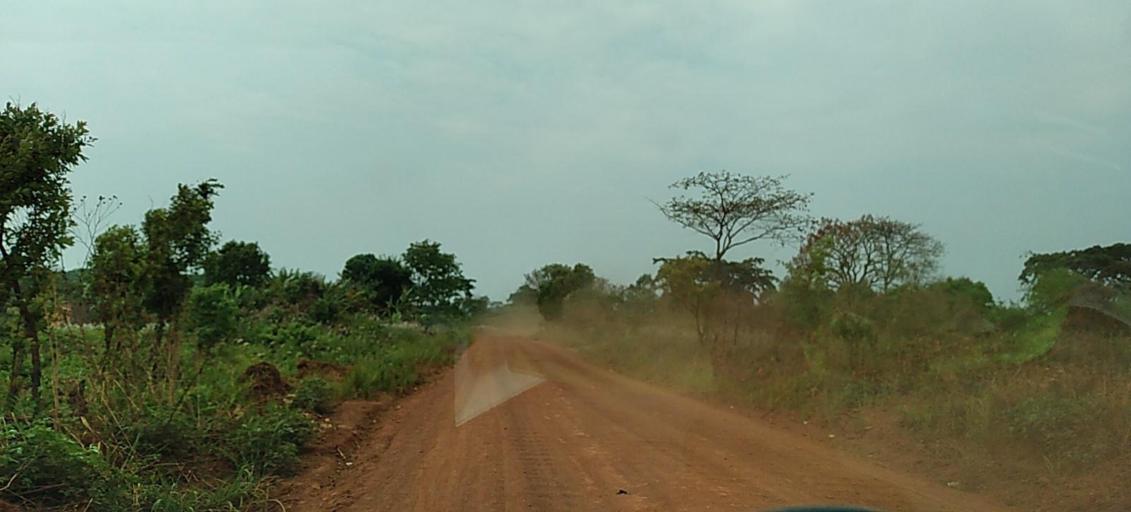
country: ZM
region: North-Western
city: Solwezi
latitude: -12.2296
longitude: 26.5111
